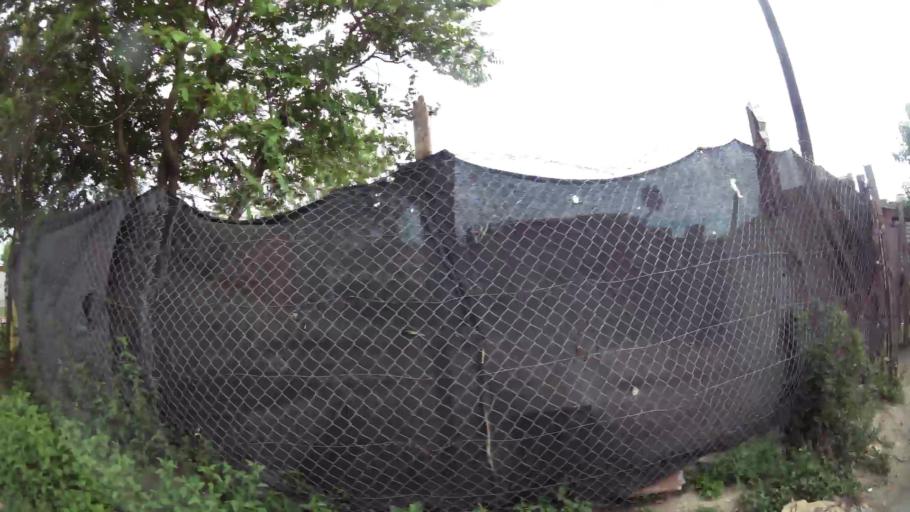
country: AR
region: Santa Fe
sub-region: Departamento de Rosario
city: Rosario
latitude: -32.9783
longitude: -60.6879
